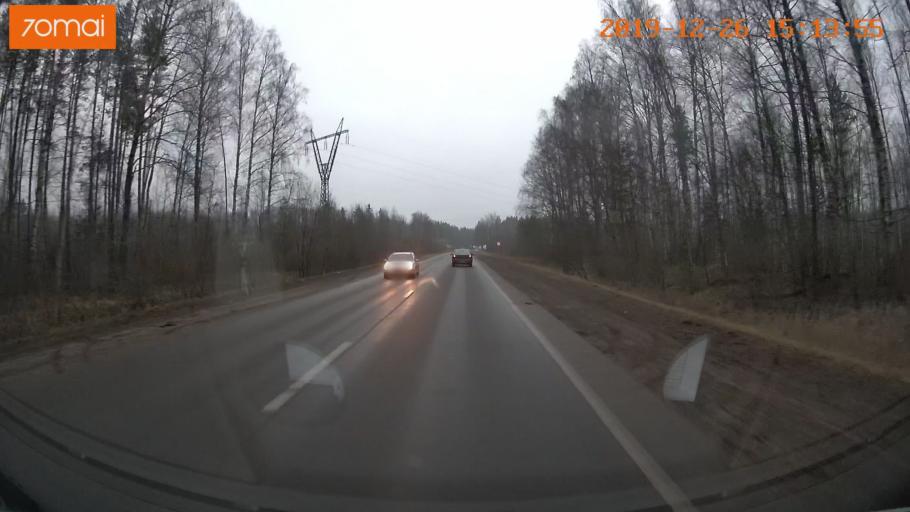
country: RU
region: Jaroslavl
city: Rybinsk
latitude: 58.1111
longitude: 38.8823
